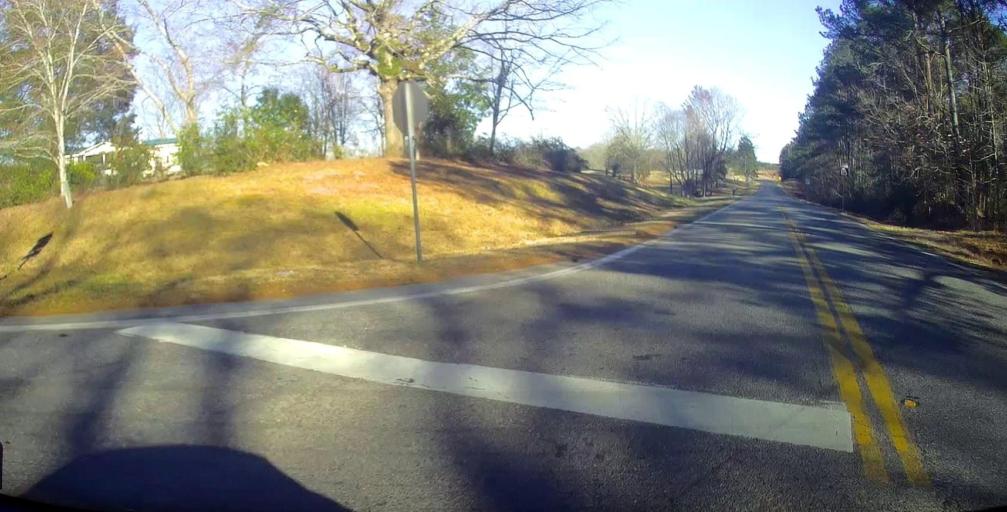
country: US
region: Georgia
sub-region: Talbot County
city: Sardis
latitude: 32.7879
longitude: -84.6444
